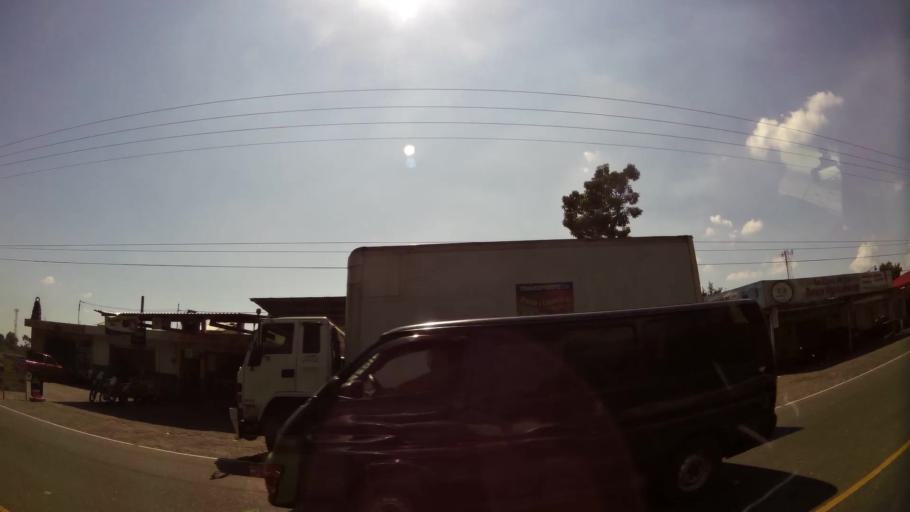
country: GT
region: Suchitepeque
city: Mazatenango
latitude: 14.5337
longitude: -91.4880
